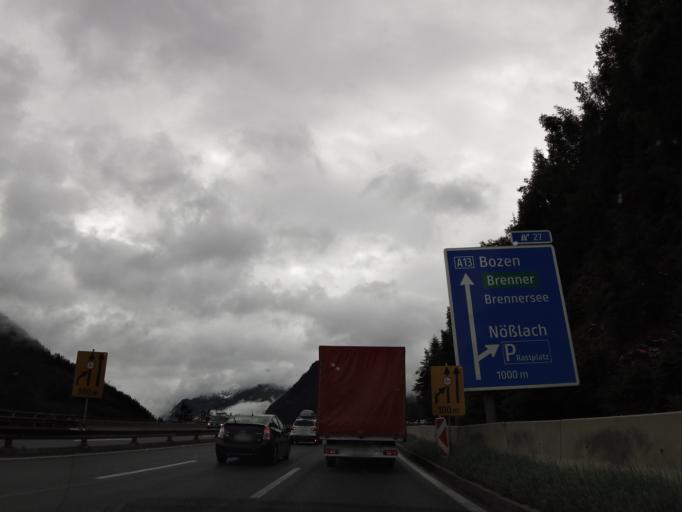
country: AT
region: Tyrol
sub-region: Politischer Bezirk Innsbruck Land
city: Steinach am Brenner
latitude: 47.0734
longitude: 11.4791
